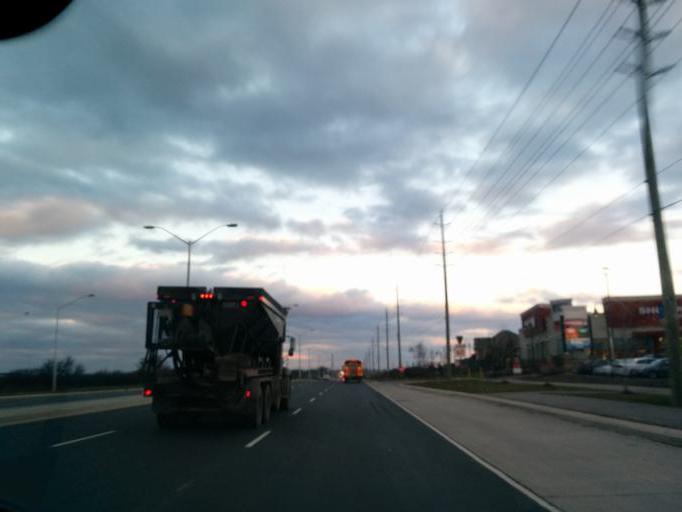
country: CA
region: Ontario
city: Oakville
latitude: 43.4982
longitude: -79.7081
